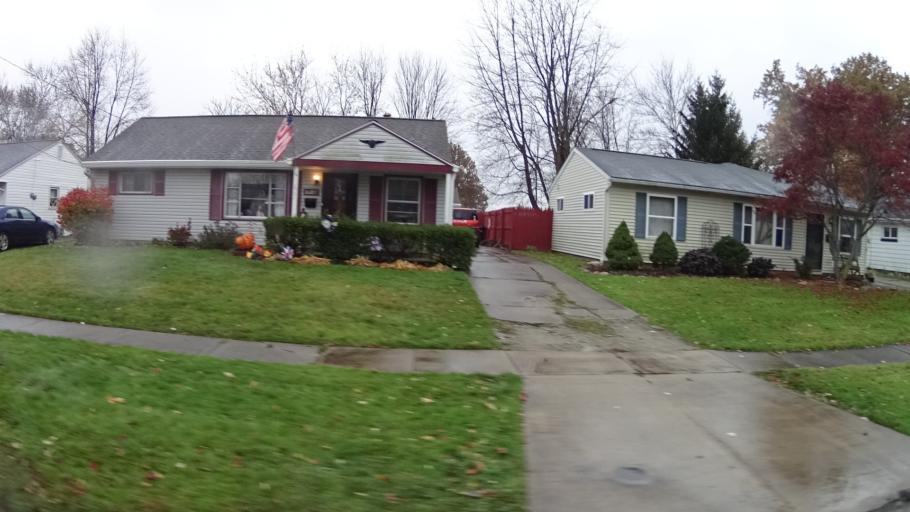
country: US
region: Ohio
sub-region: Lorain County
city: Elyria
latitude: 41.3816
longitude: -82.1340
